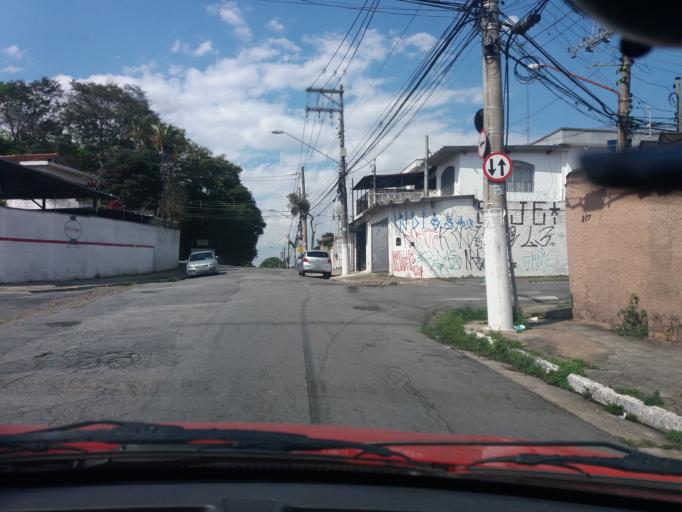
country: BR
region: Sao Paulo
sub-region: Taboao Da Serra
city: Taboao da Serra
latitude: -23.5881
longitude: -46.7350
